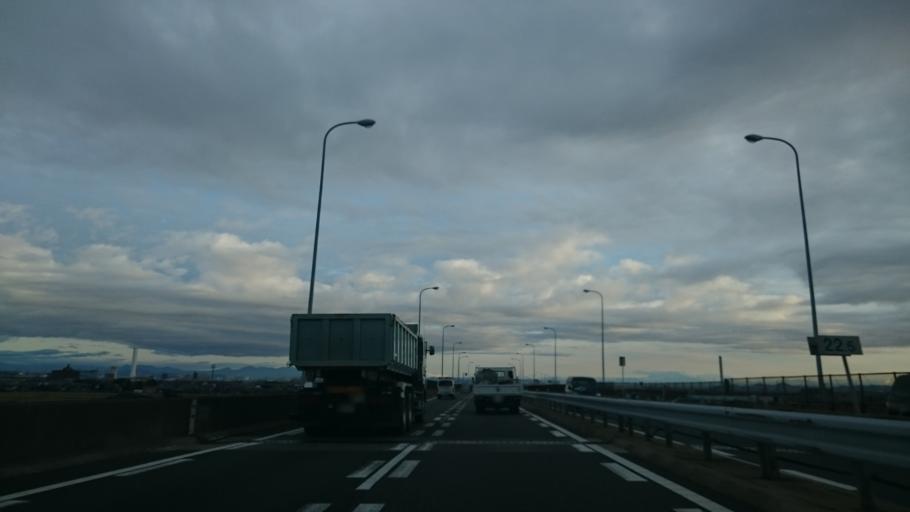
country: JP
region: Aichi
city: Inazawa
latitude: 35.2091
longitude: 136.8230
